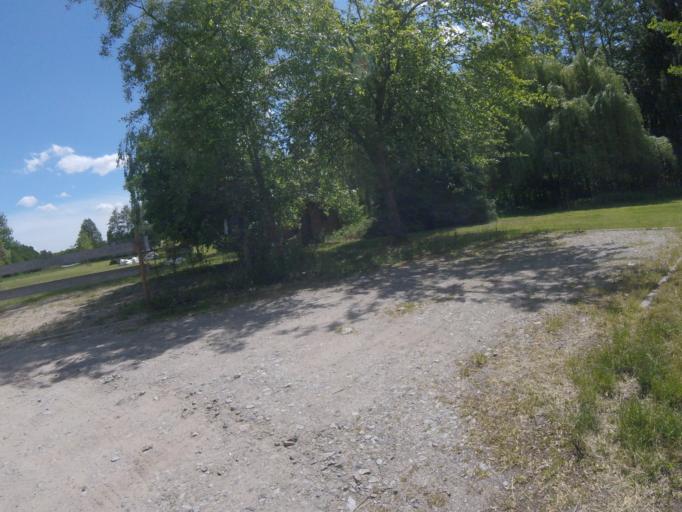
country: DE
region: Brandenburg
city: Schwerin
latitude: 52.1504
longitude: 13.6306
